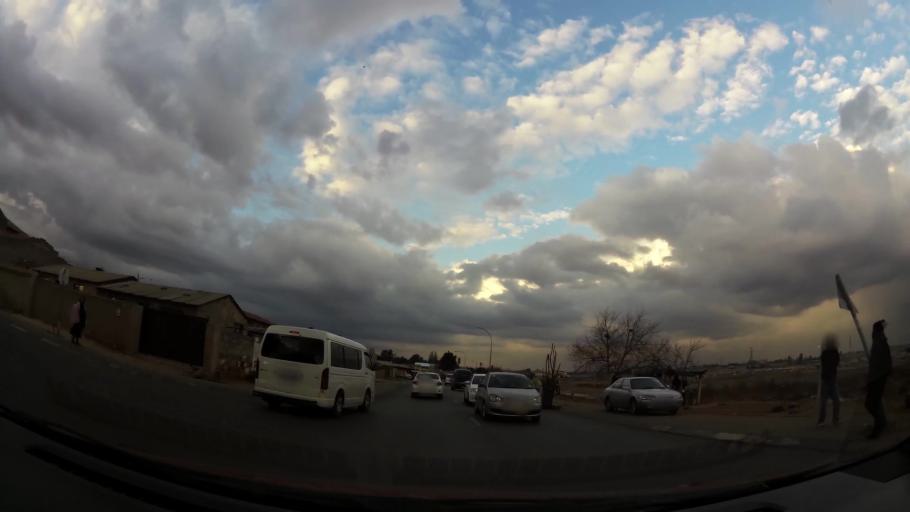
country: ZA
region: Gauteng
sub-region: City of Johannesburg Metropolitan Municipality
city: Soweto
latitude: -26.2412
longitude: 27.8404
